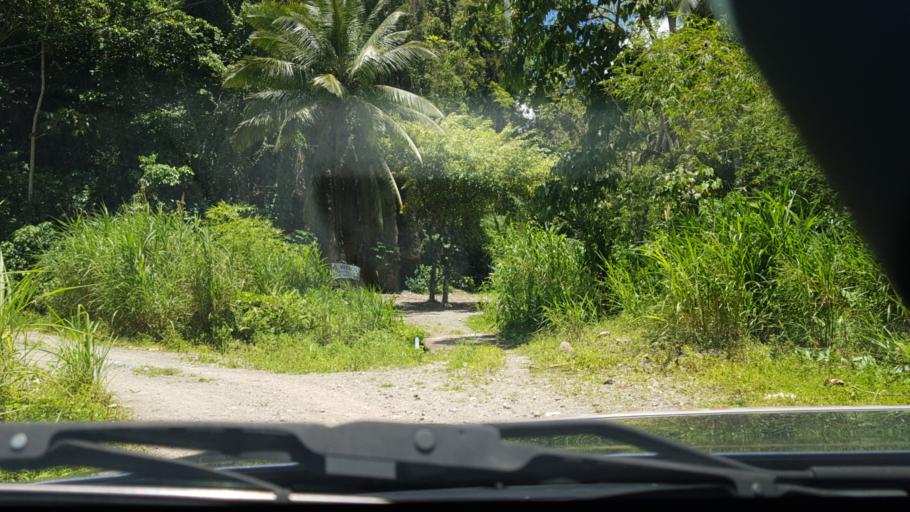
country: LC
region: Anse-la-Raye
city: Canaries
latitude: 13.8984
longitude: -61.0586
